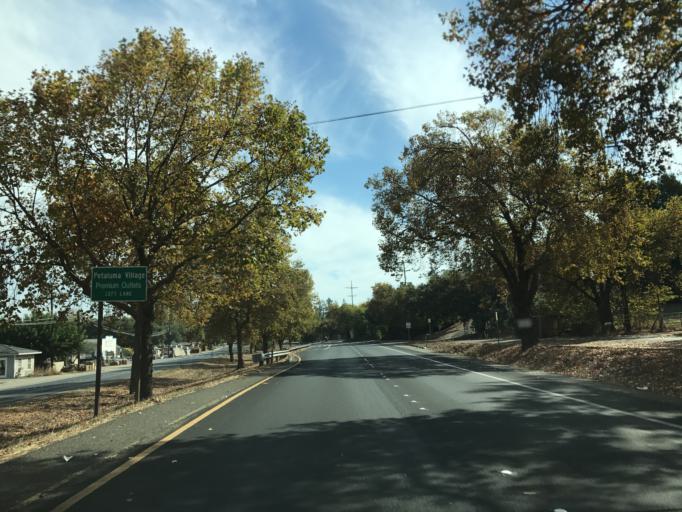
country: US
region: California
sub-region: Sonoma County
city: Petaluma
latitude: 38.2569
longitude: -122.6542
